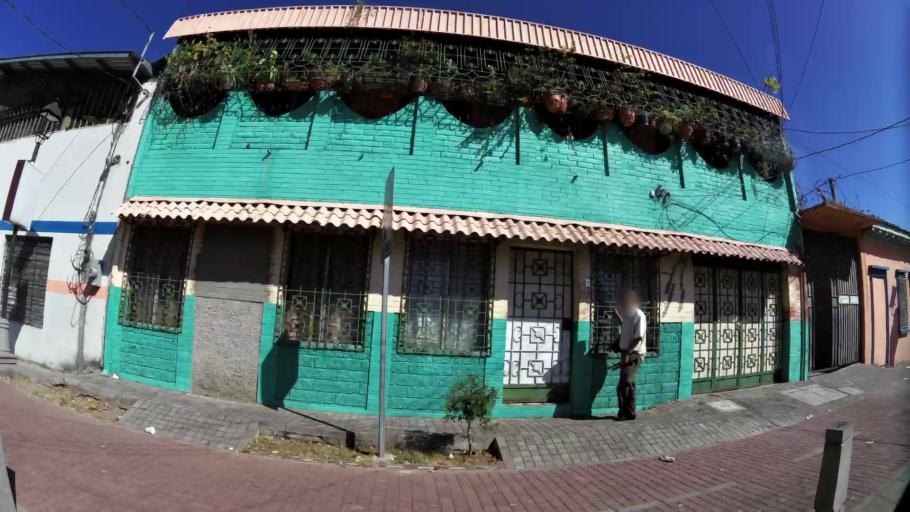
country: SV
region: La Libertad
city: Santa Tecla
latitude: 13.6756
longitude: -89.2942
